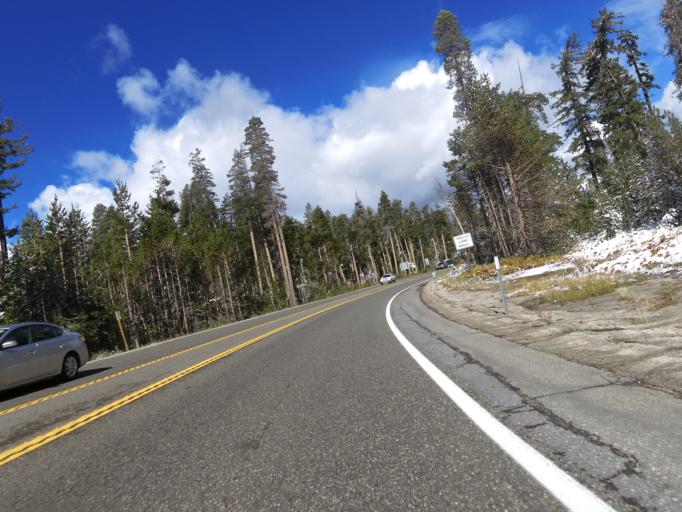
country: US
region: California
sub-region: El Dorado County
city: South Lake Tahoe
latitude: 38.8133
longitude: -120.0324
